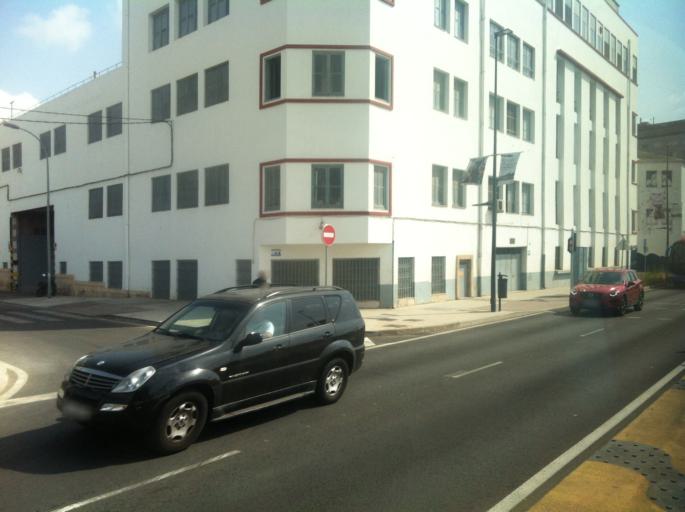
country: ES
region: Valencia
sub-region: Provincia de Alicante
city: Alicante
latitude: 38.3380
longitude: -0.4971
